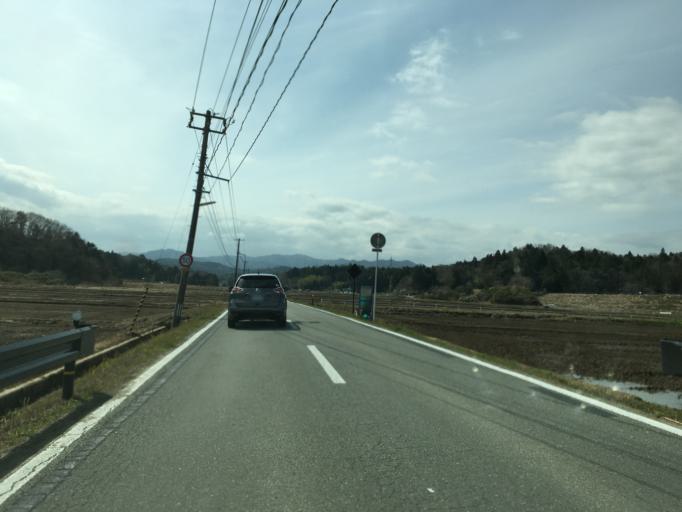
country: JP
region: Fukushima
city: Namie
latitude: 37.4569
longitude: 140.9908
